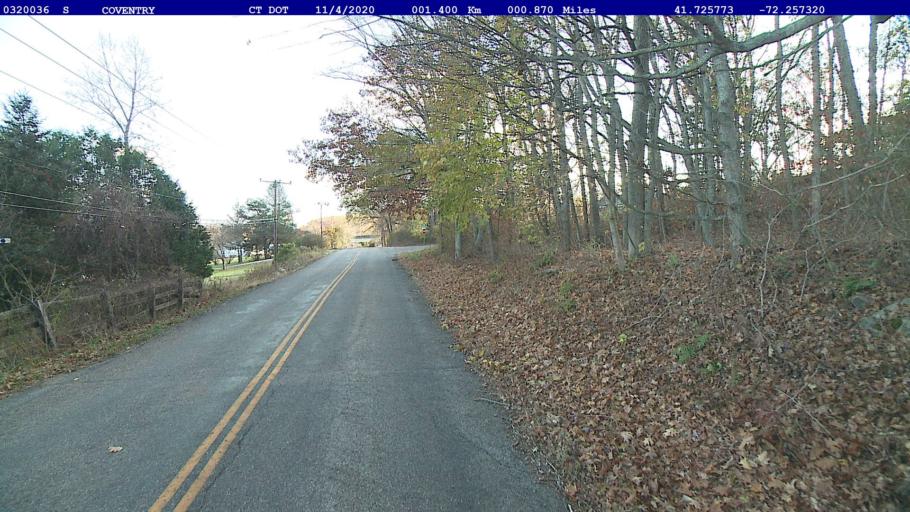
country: US
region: Connecticut
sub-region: Tolland County
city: Mansfield City
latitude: 41.7258
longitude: -72.2573
